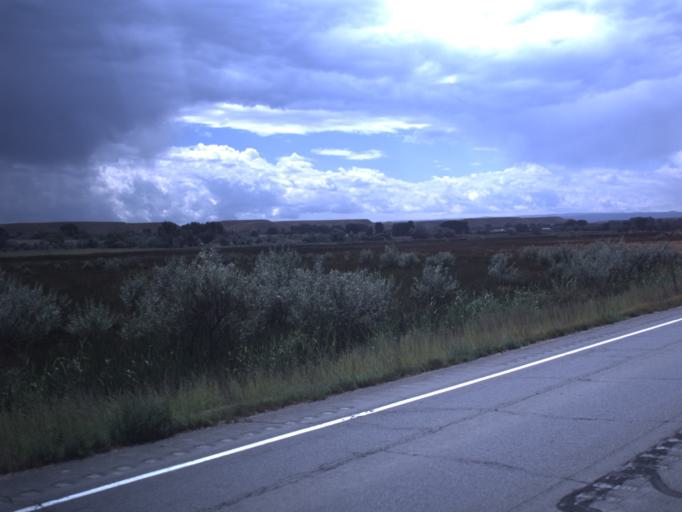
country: US
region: Utah
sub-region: Duchesne County
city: Roosevelt
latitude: 40.1633
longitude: -110.1588
